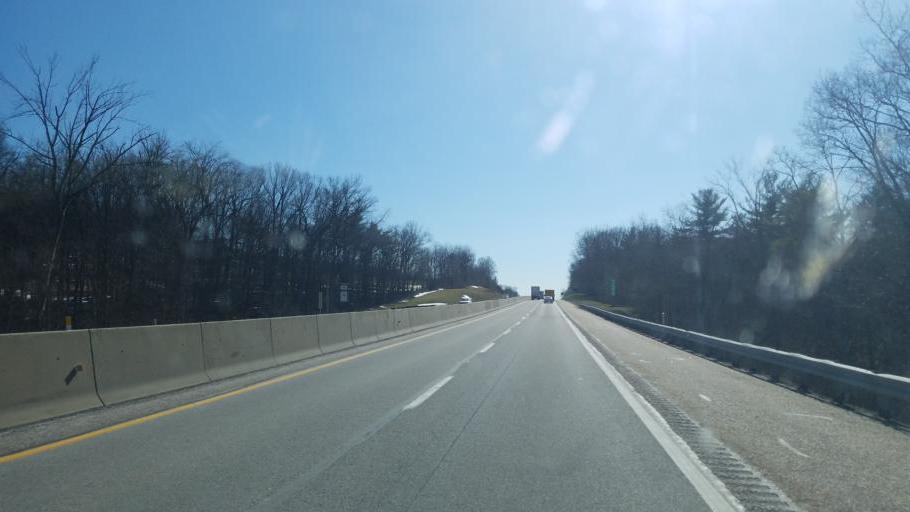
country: US
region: Pennsylvania
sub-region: Franklin County
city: Doylestown
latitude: 40.1554
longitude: -77.7095
